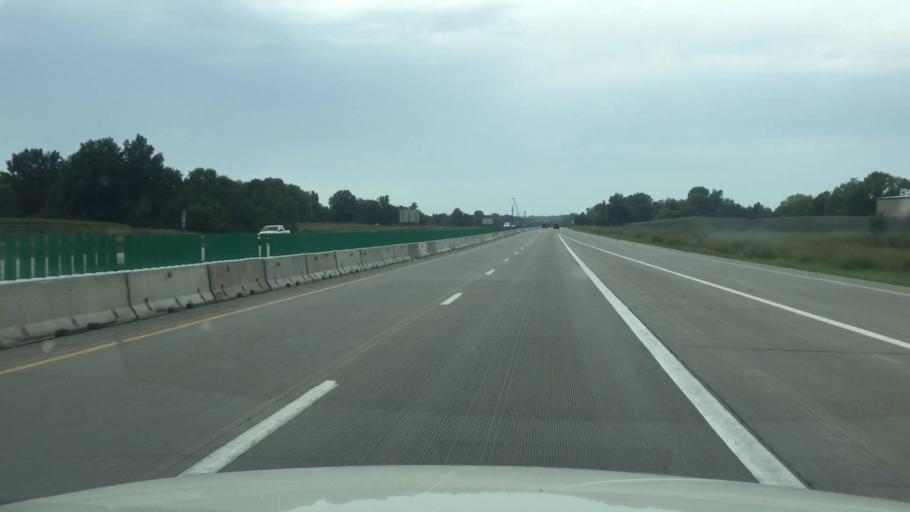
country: US
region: Iowa
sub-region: Polk County
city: Ankeny
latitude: 41.7554
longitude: -93.5717
